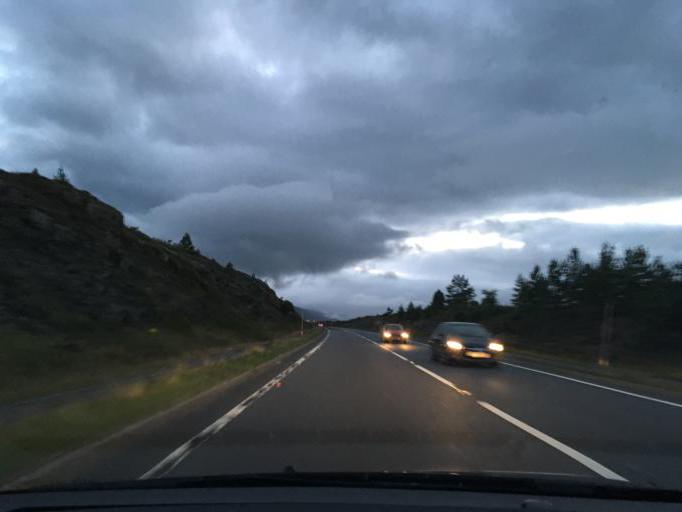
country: GB
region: Scotland
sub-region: Highland
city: Kingussie
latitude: 56.9626
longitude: -4.2036
